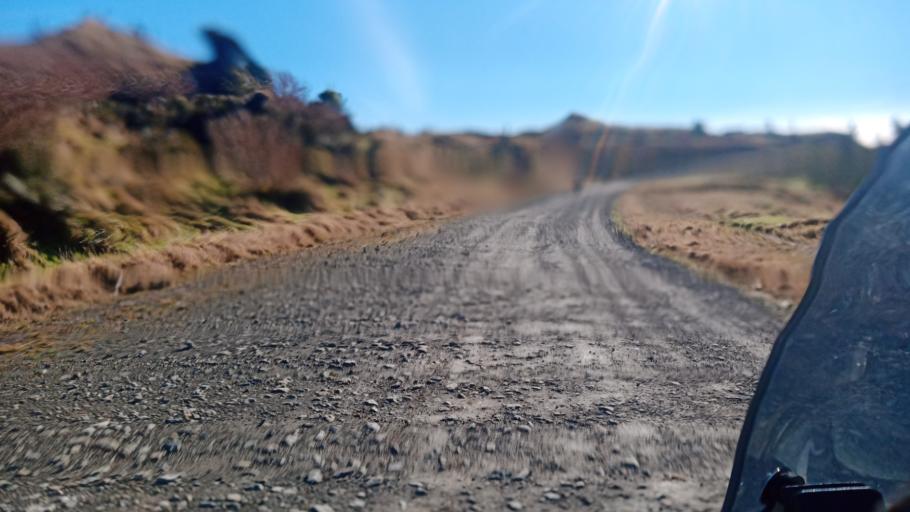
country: NZ
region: Gisborne
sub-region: Gisborne District
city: Gisborne
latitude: -38.1875
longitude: 177.8192
